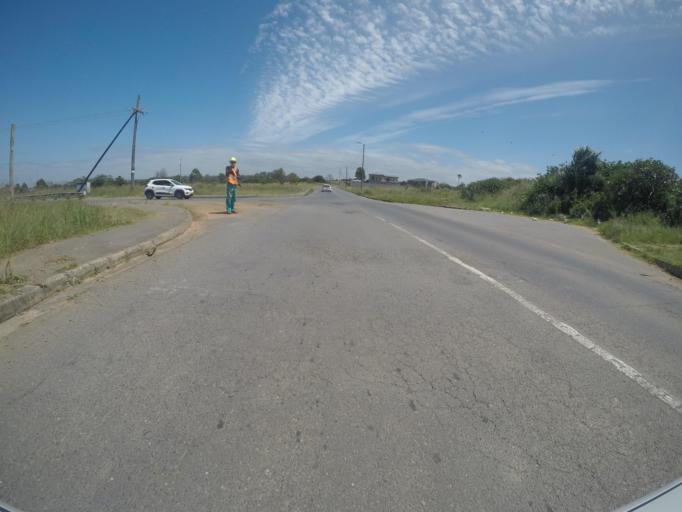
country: ZA
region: Eastern Cape
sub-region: Buffalo City Metropolitan Municipality
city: East London
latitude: -32.9456
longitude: 27.9950
